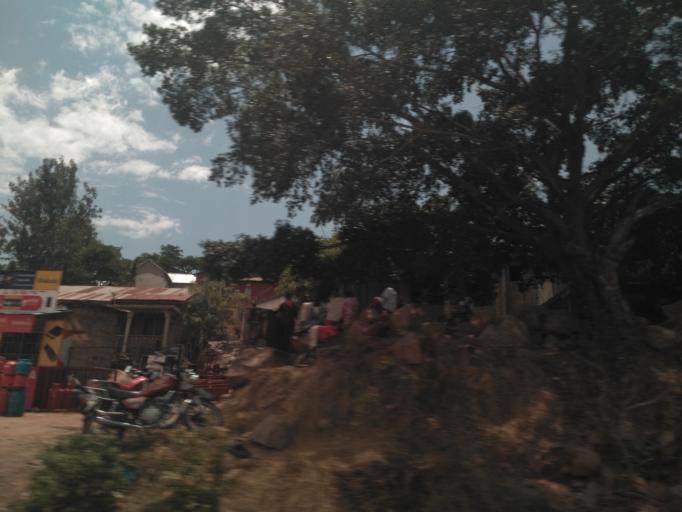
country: TZ
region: Mwanza
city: Mwanza
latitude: -2.4803
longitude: 32.9090
